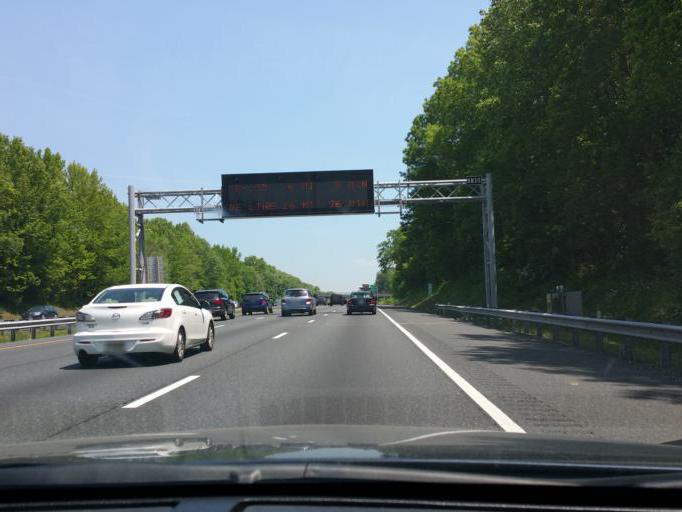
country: US
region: Maryland
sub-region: Harford County
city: Perryman
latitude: 39.5094
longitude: -76.2104
